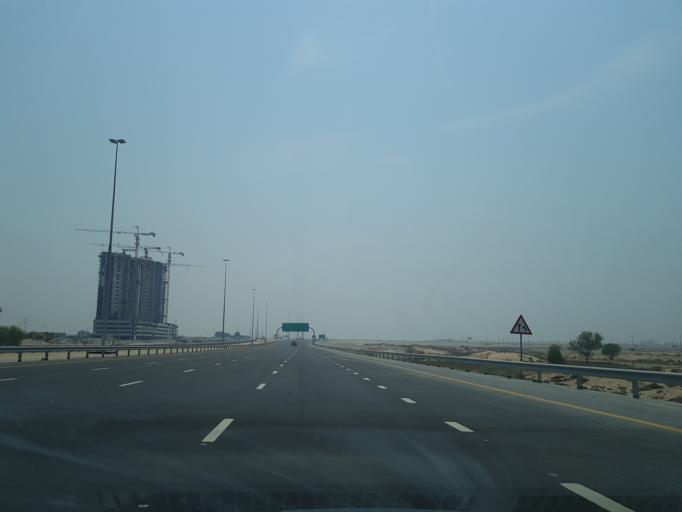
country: AE
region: Dubai
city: Dubai
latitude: 25.0288
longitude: 55.2476
